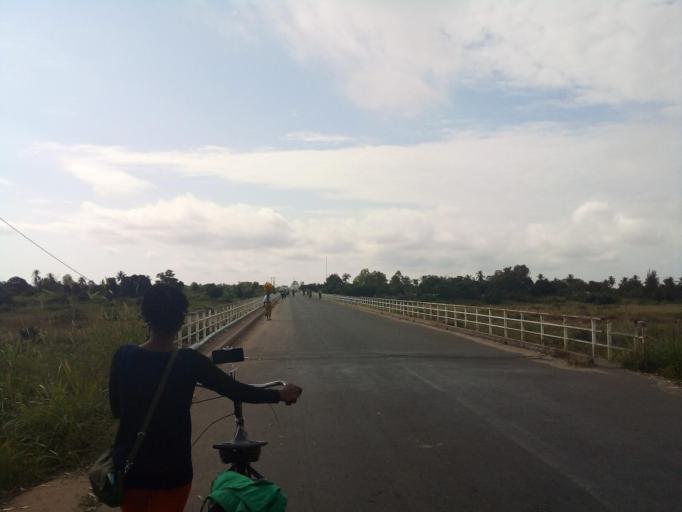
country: MZ
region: Zambezia
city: Quelimane
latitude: -17.5778
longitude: 36.6898
